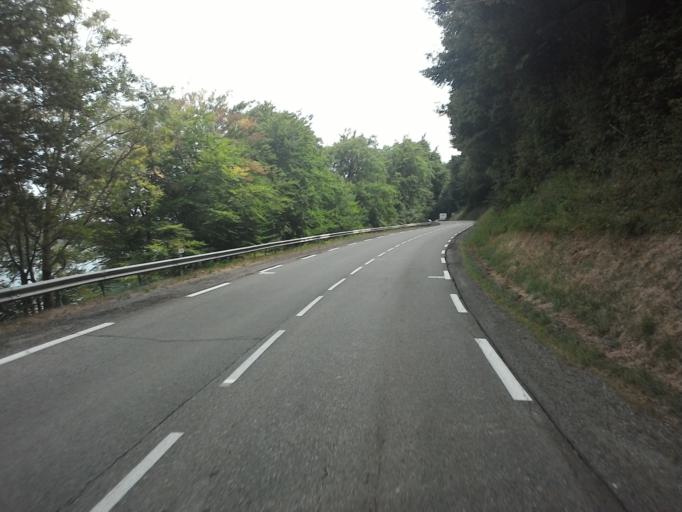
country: FR
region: Rhone-Alpes
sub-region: Departement de l'Isere
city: Pierre-Chatel
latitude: 45.0056
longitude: 5.7724
